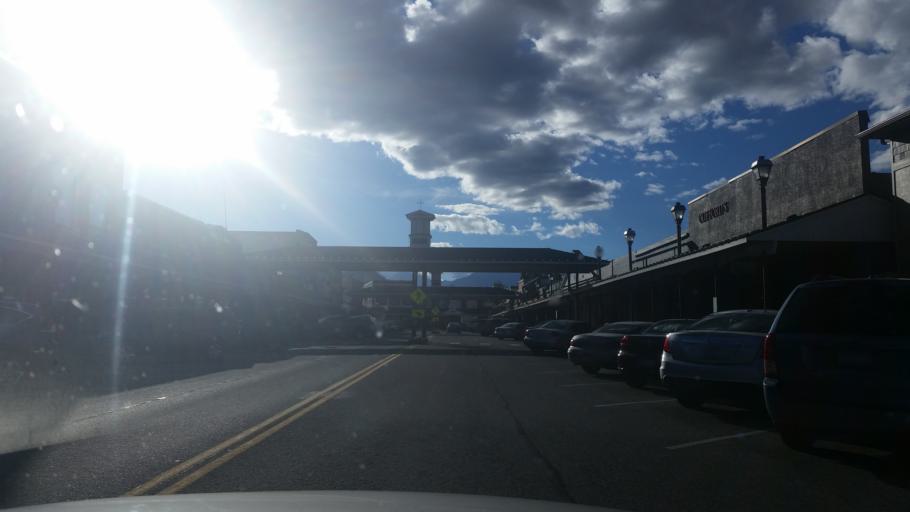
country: US
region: Washington
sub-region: Chelan County
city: Cashmere
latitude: 47.5220
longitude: -120.4682
